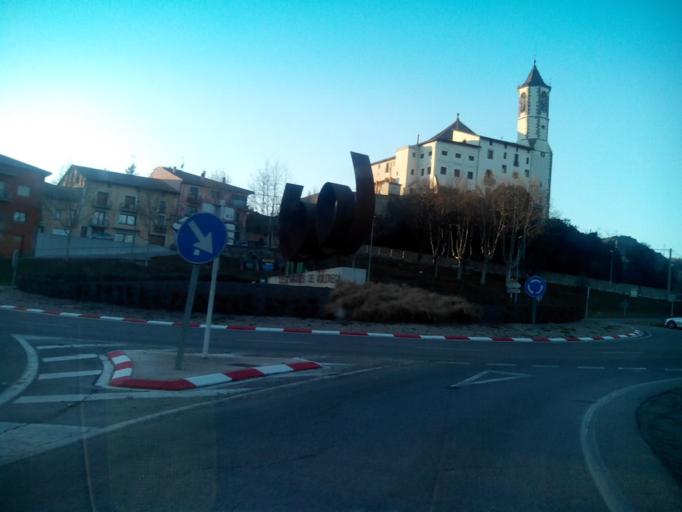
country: ES
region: Catalonia
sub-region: Provincia de Barcelona
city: Santa Cecilia de Voltrega
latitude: 42.0027
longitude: 2.2428
